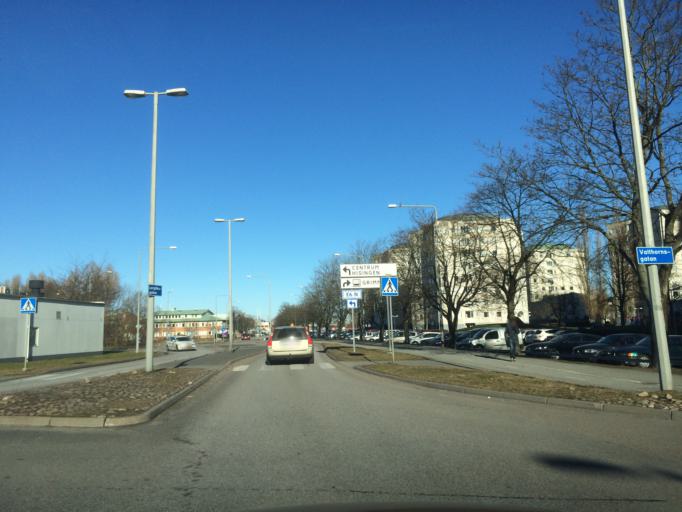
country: SE
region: Vaestra Goetaland
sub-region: Goteborg
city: Majorna
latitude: 57.6526
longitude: 11.9070
